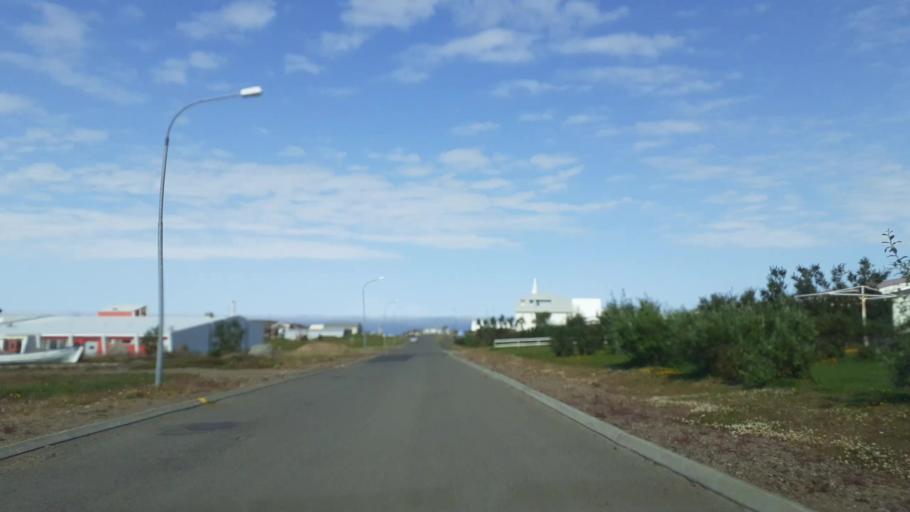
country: IS
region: Northwest
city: Saudarkrokur
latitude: 65.8208
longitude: -20.3023
